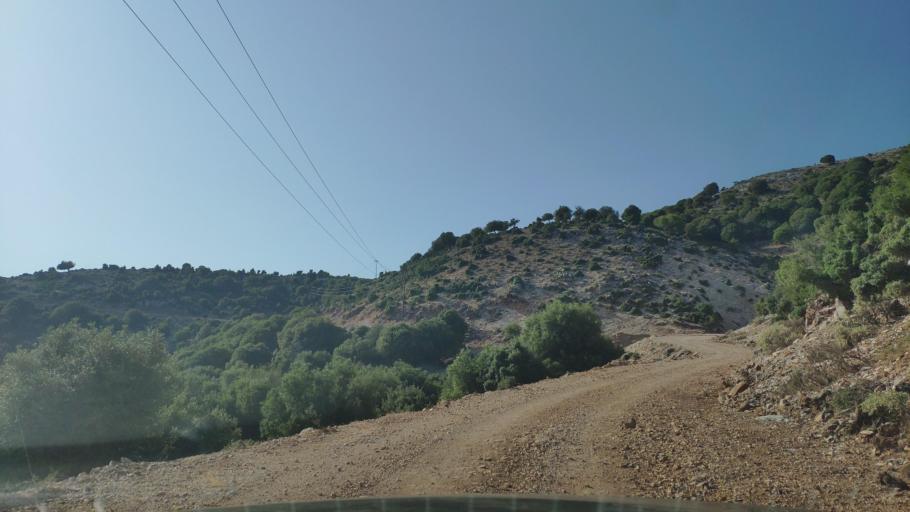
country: GR
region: West Greece
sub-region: Nomos Aitolias kai Akarnanias
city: Monastirakion
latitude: 38.8323
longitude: 20.9729
